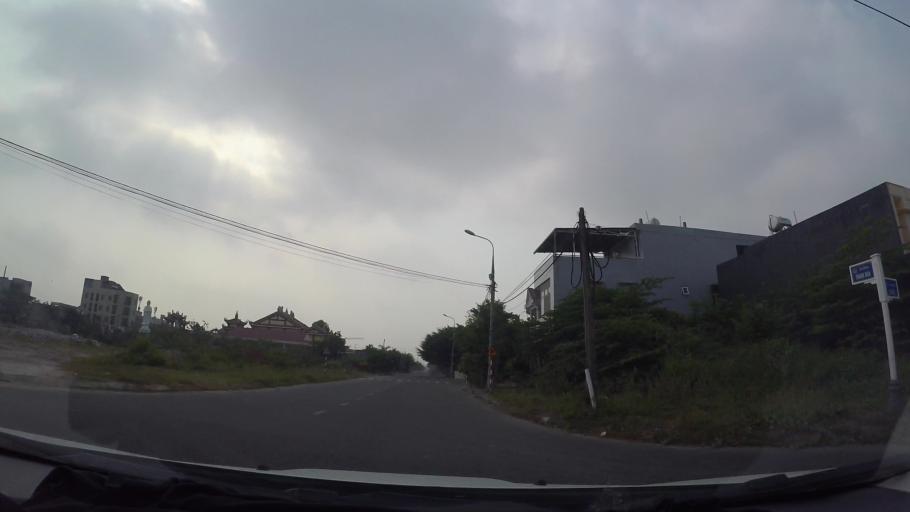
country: VN
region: Da Nang
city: Cam Le
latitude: 16.0062
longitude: 108.2178
